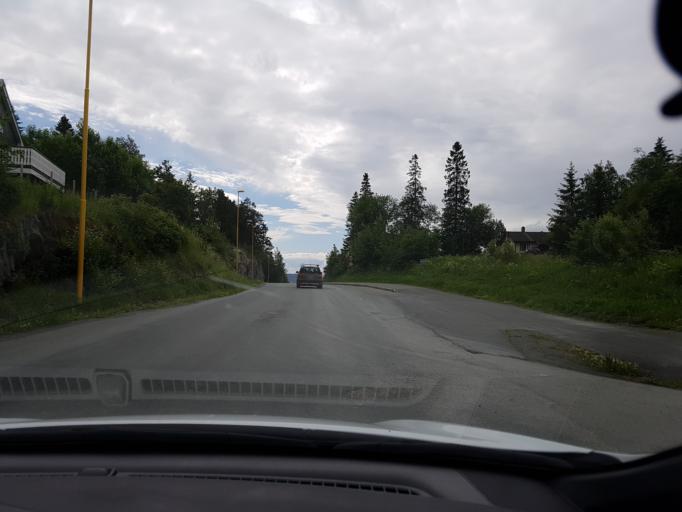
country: NO
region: Nord-Trondelag
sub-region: Frosta
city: Frosta
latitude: 63.5950
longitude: 10.7361
